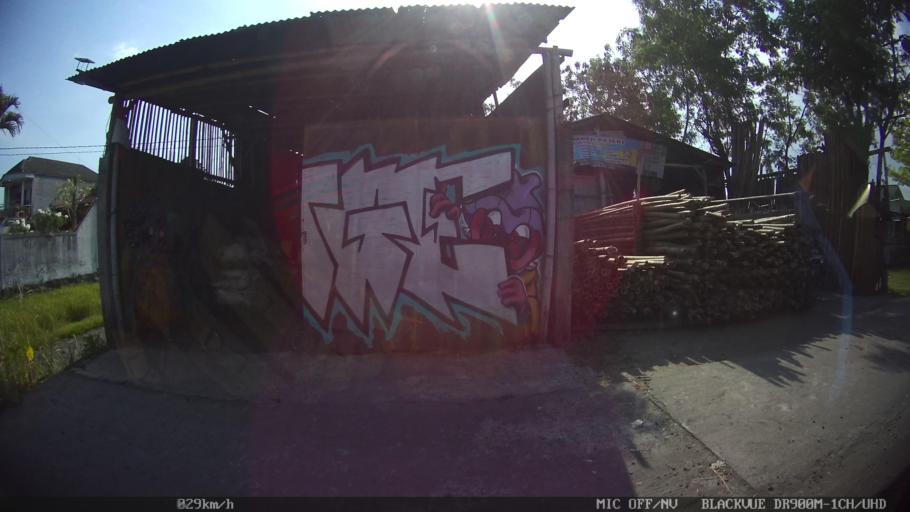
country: ID
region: Daerah Istimewa Yogyakarta
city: Kasihan
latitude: -7.8459
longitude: 110.3429
